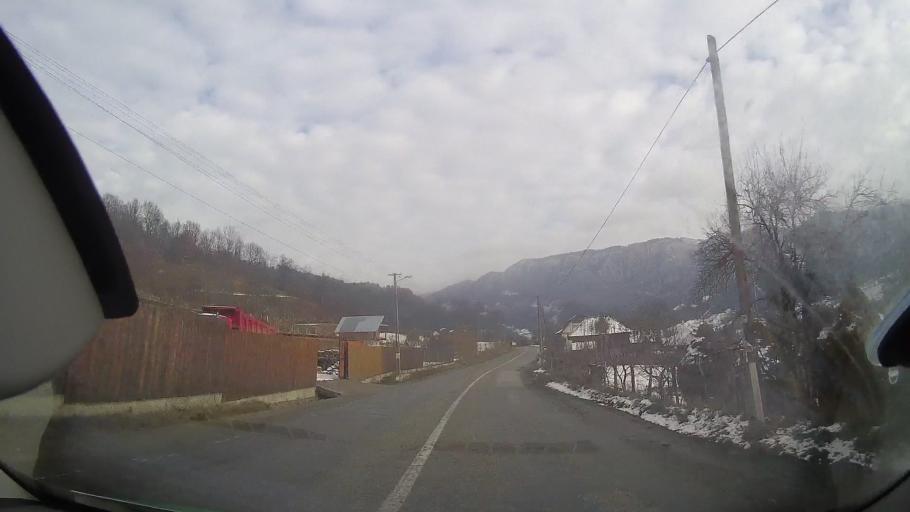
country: RO
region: Alba
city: Salciua de Sus
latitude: 46.4013
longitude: 23.4293
